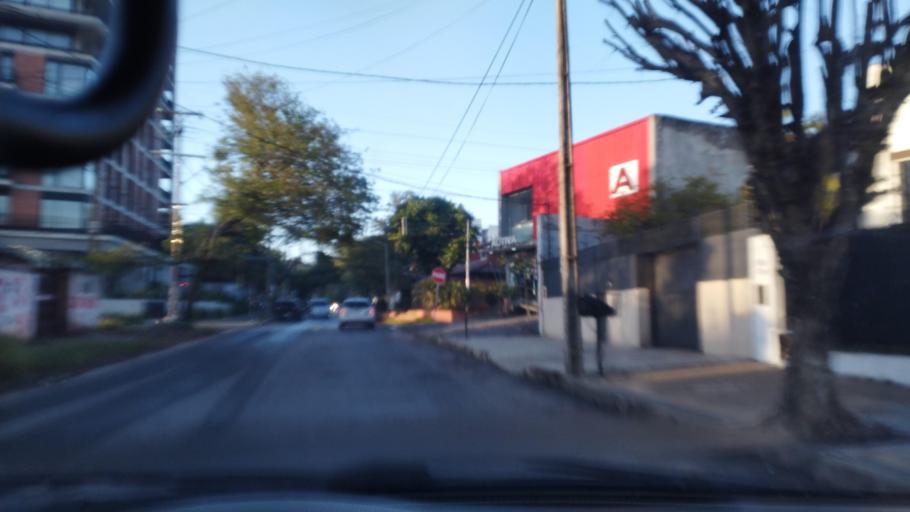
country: PY
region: Central
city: Fernando de la Mora
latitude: -25.2916
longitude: -57.5545
